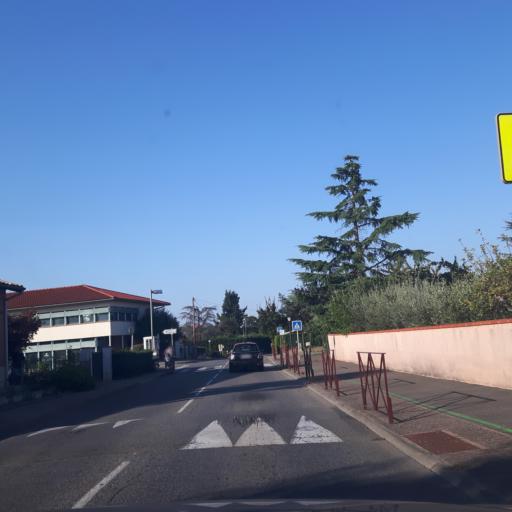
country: FR
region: Midi-Pyrenees
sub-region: Departement de la Haute-Garonne
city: Bouloc
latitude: 43.7824
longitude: 1.4083
